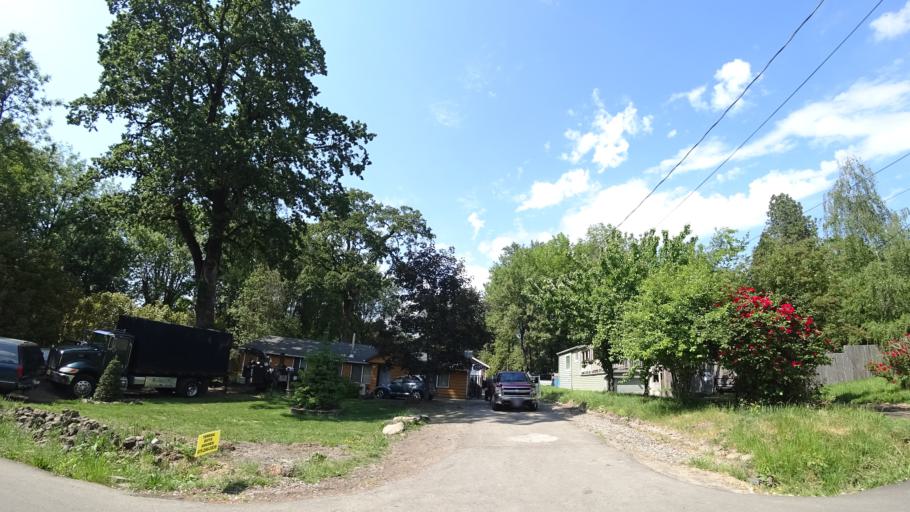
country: US
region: Oregon
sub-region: Washington County
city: Metzger
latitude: 45.4511
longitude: -122.7440
